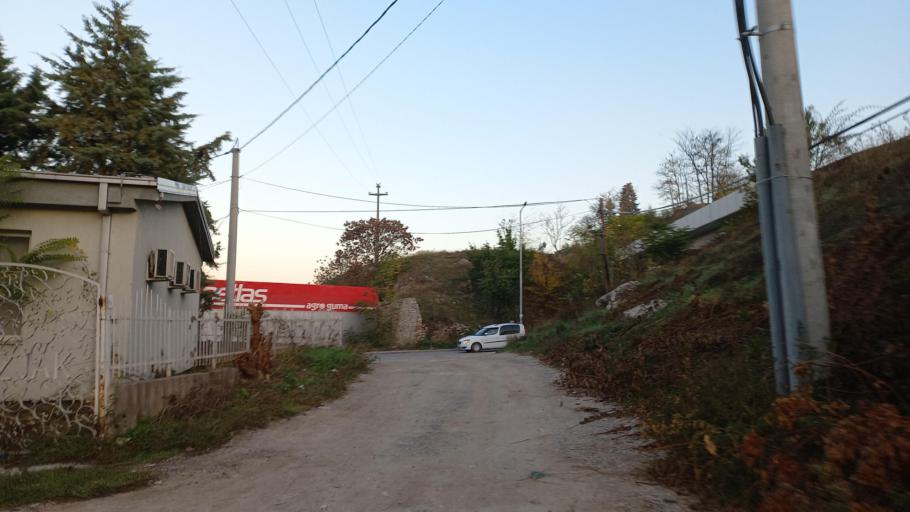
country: MK
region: Kumanovo
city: Kumanovo
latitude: 42.1431
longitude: 21.7228
